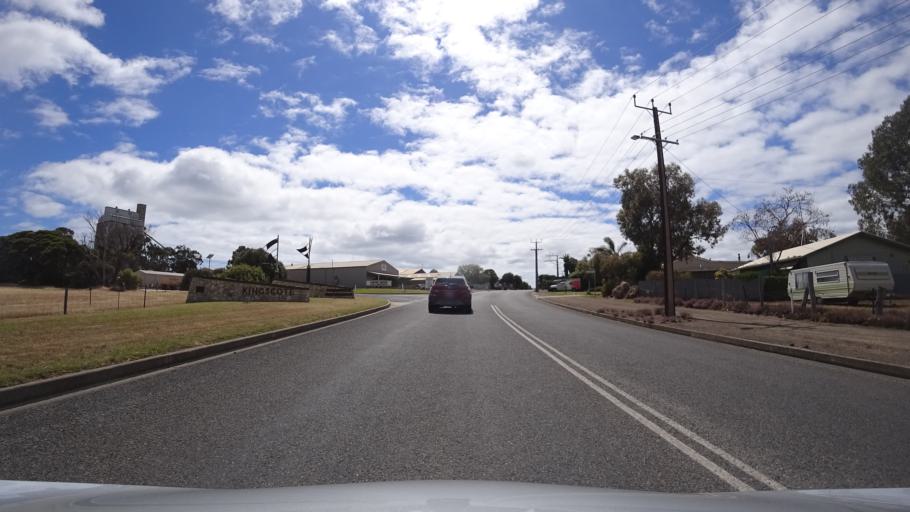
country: AU
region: South Australia
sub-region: Kangaroo Island
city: Kingscote
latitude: -35.6526
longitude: 137.6274
